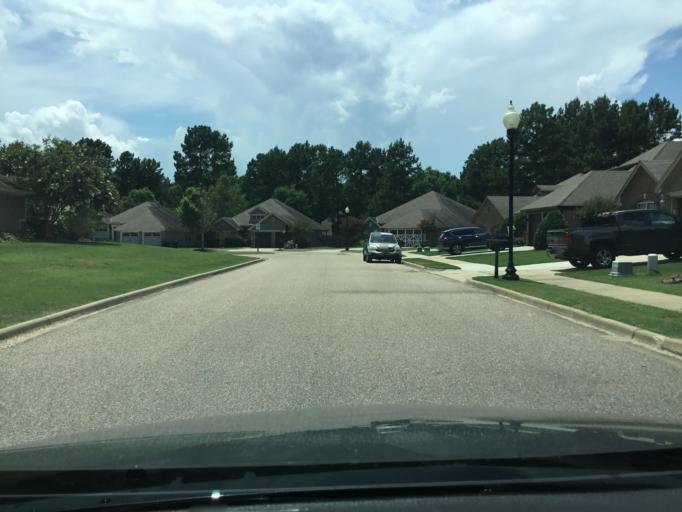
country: US
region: Alabama
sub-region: Montgomery County
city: Pike Road
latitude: 32.3408
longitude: -86.0816
